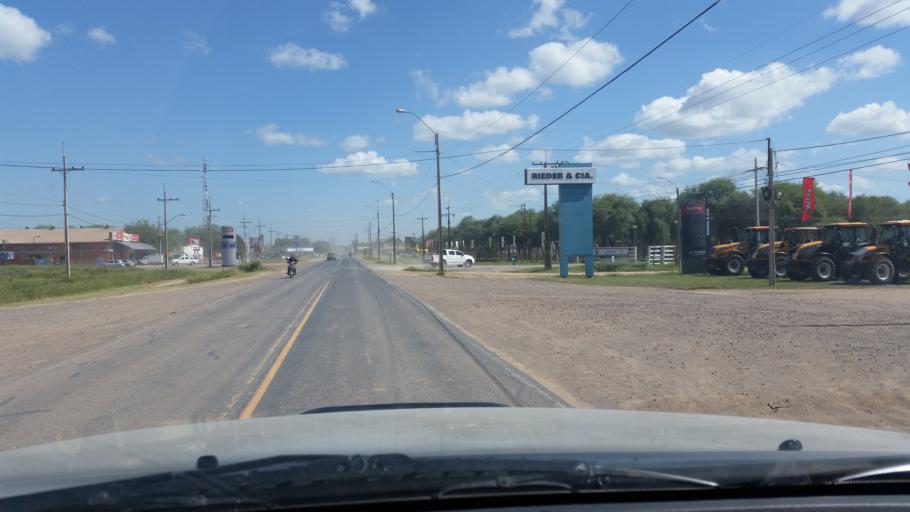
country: PY
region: Boqueron
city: Colonia Menno
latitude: -22.3918
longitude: -59.8364
